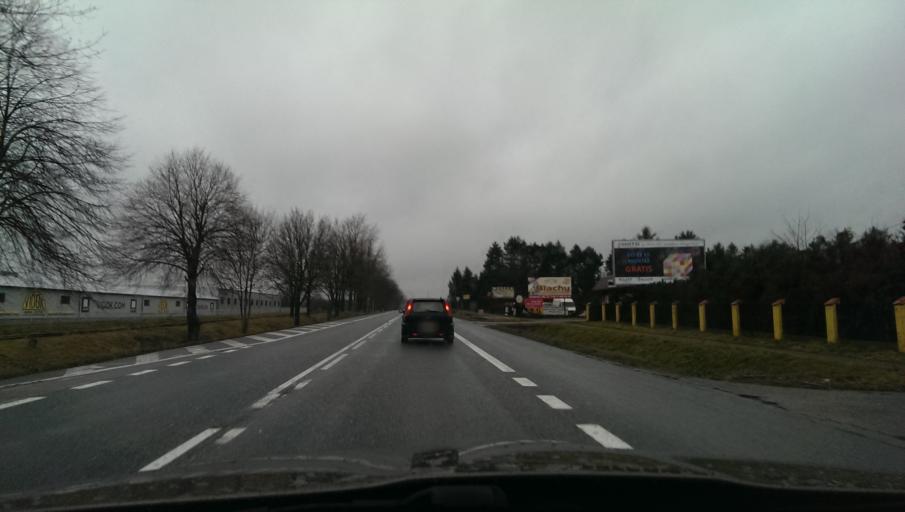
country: PL
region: Subcarpathian Voivodeship
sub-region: Powiat rzeszowski
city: Rudna Mala
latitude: 50.1022
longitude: 21.9777
